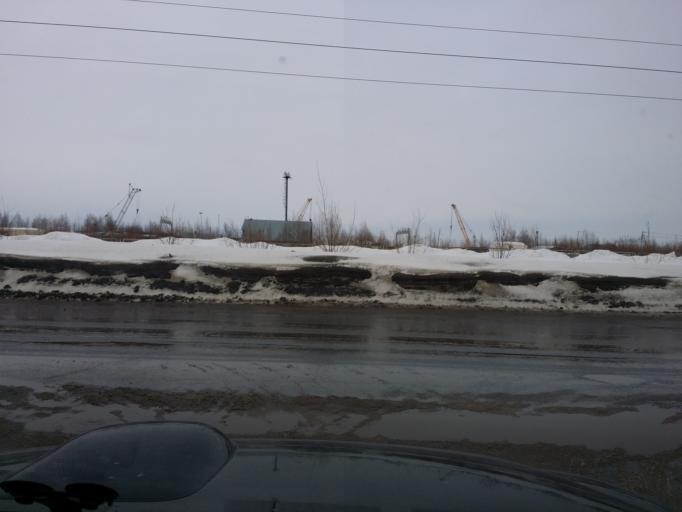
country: RU
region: Khanty-Mansiyskiy Avtonomnyy Okrug
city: Nizhnevartovsk
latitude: 60.9574
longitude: 76.5811
